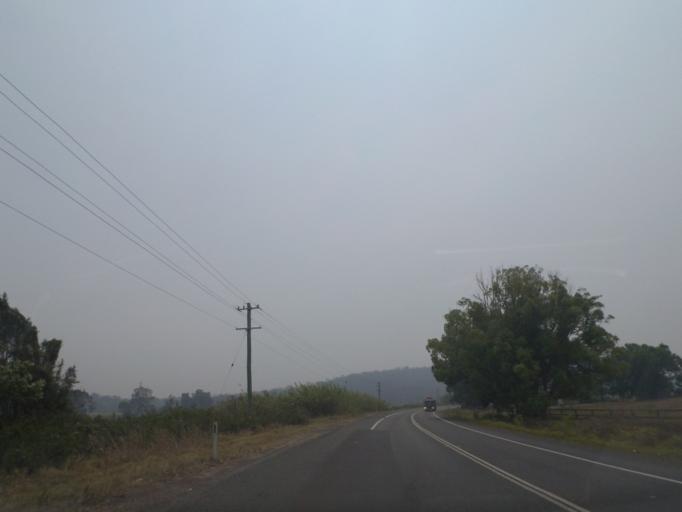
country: AU
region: New South Wales
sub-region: Clarence Valley
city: Maclean
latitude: -29.5445
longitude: 153.1558
